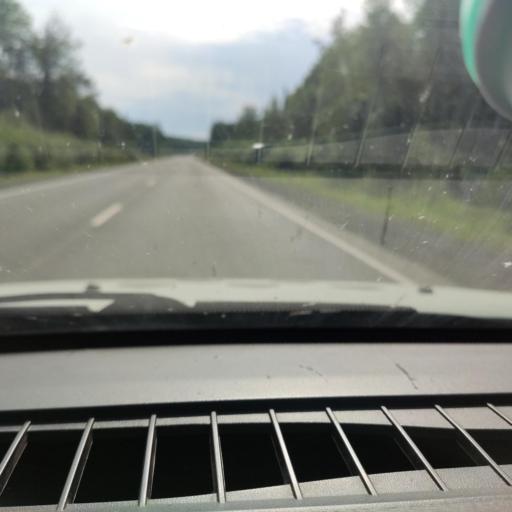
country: RU
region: Perm
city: Zyukayka
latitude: 58.3697
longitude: 54.6615
